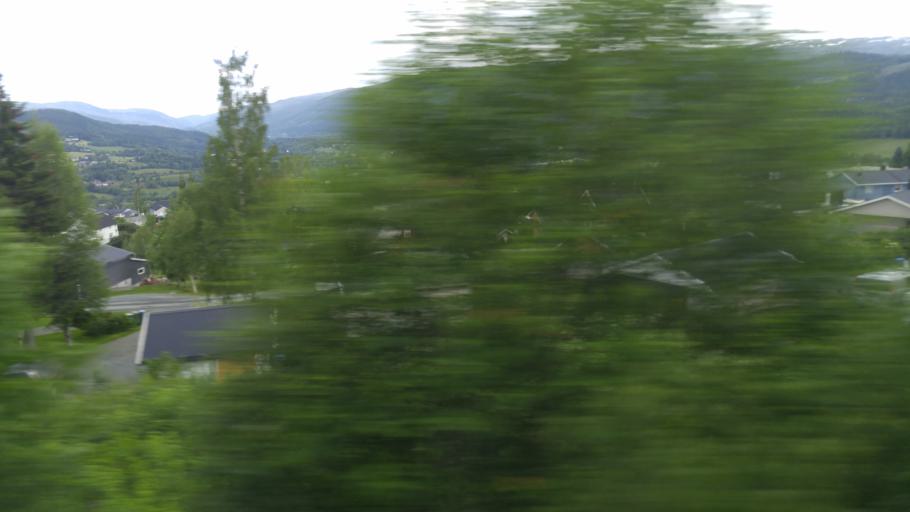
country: NO
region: Nord-Trondelag
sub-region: Meraker
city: Meraker
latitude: 63.4196
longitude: 11.7571
